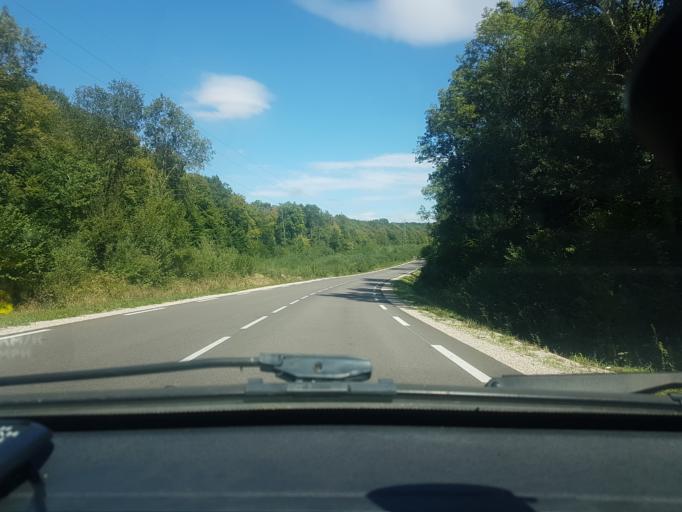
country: FR
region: Franche-Comte
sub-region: Departement de la Haute-Saone
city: Gray-la-Ville
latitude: 47.4085
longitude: 5.4955
